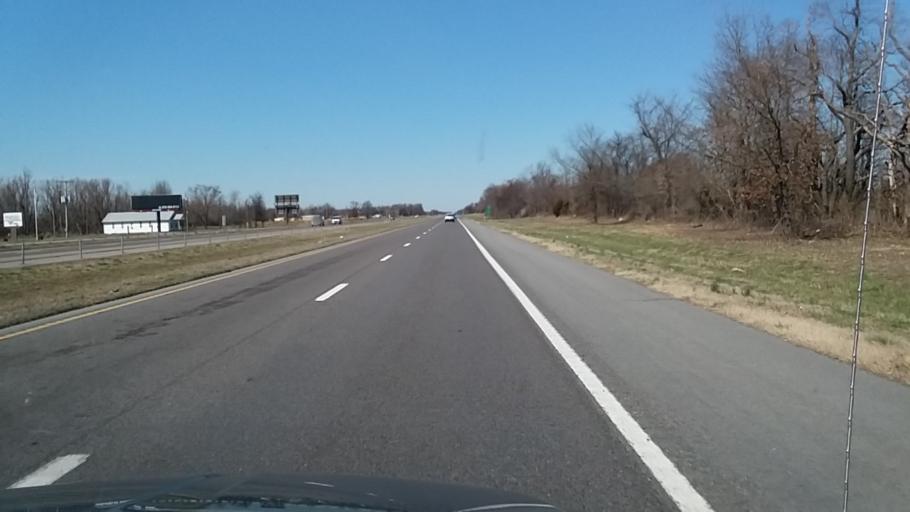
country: US
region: Missouri
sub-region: Scott County
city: Sikeston
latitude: 36.9663
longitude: -89.5342
